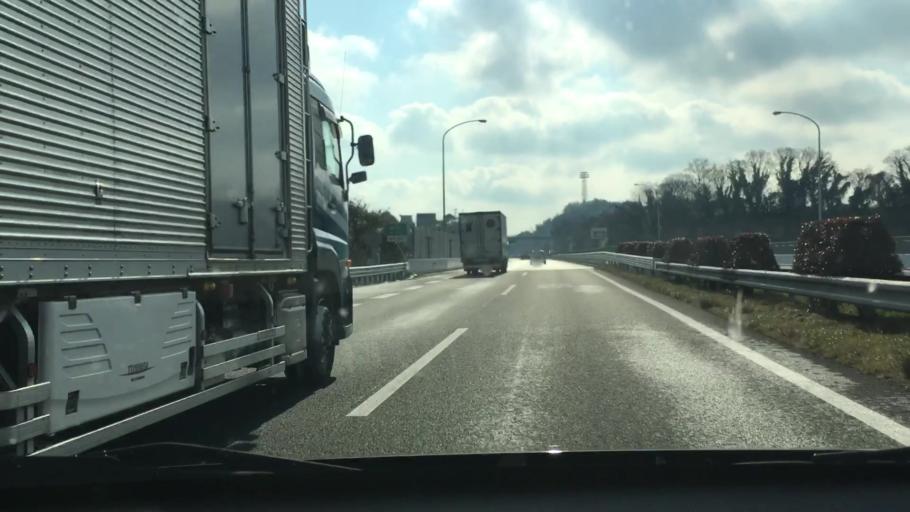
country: JP
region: Kumamoto
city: Kumamoto
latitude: 32.7317
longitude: 130.7757
